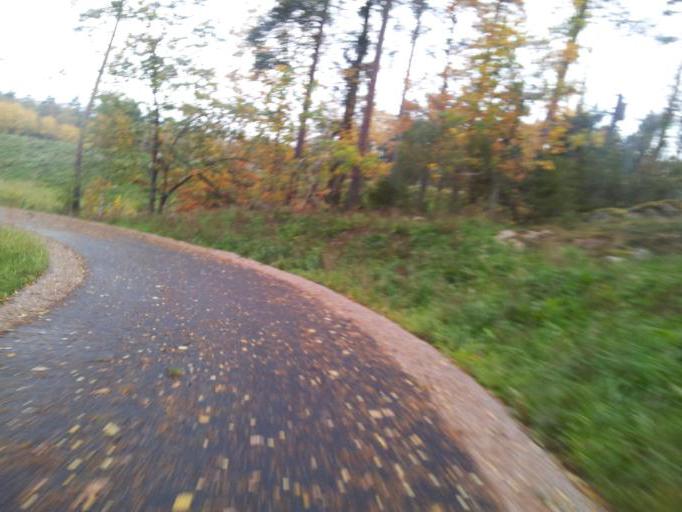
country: SE
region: Uppsala
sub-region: Uppsala Kommun
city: Storvreta
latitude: 59.9111
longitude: 17.7385
